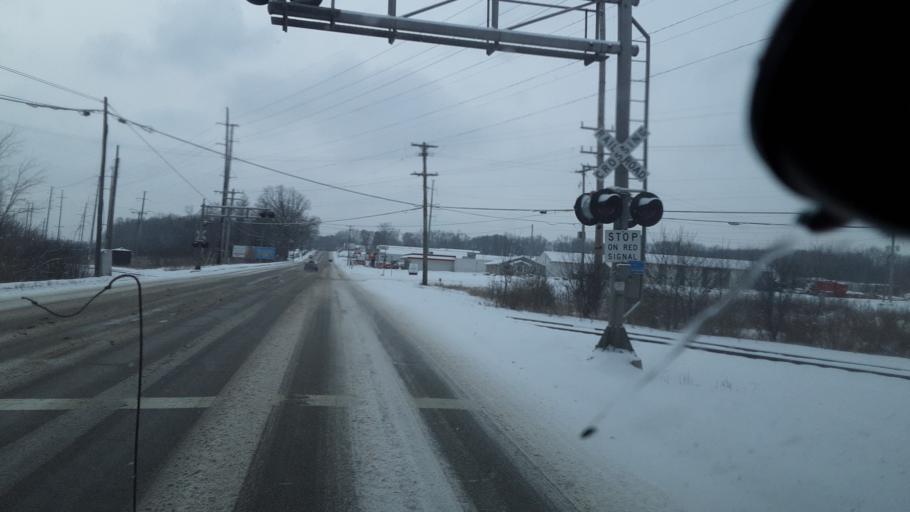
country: US
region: Michigan
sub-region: Jackson County
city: Jackson
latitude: 42.2831
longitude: -84.4137
